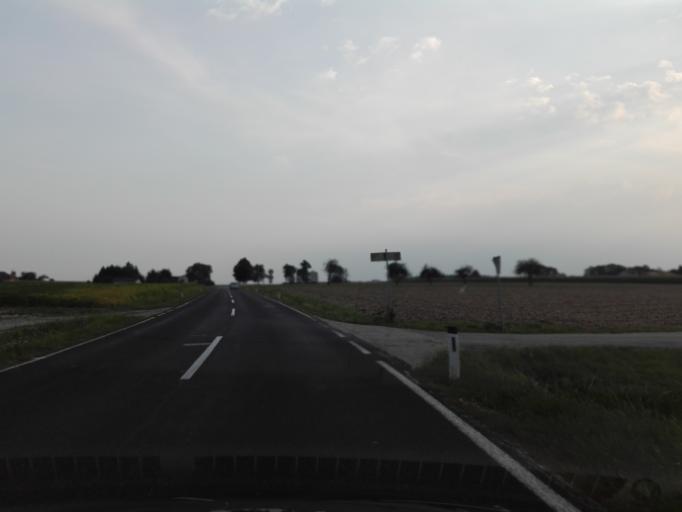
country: AT
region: Upper Austria
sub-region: Politischer Bezirk Grieskirchen
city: Grieskirchen
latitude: 48.2666
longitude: 13.8150
